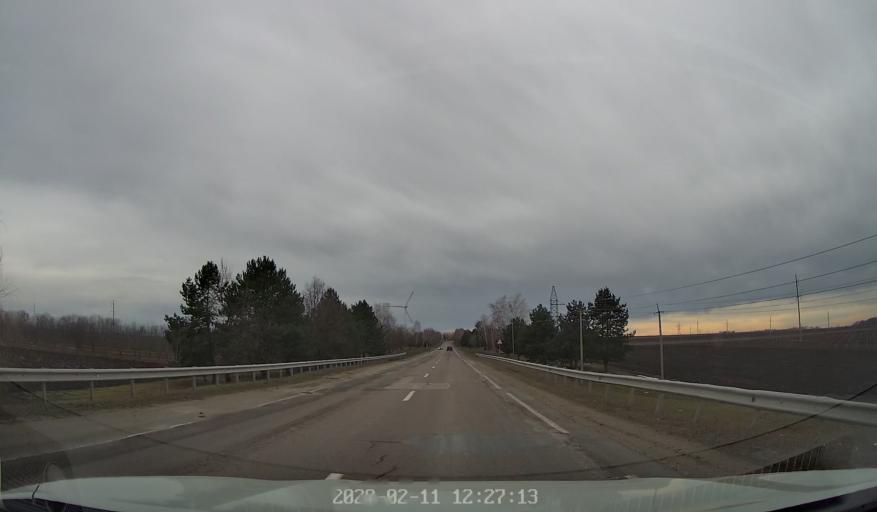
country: MD
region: Raionul Edinet
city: Edinet
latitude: 48.1509
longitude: 27.3190
